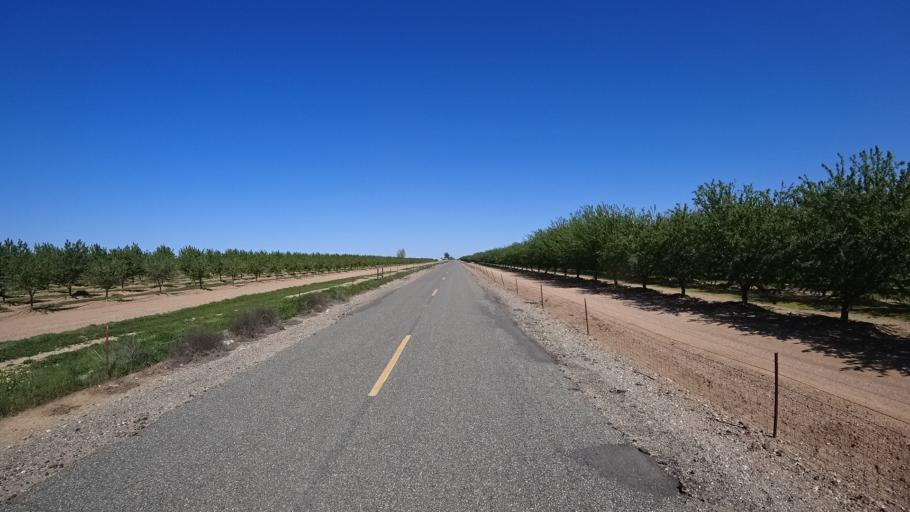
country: US
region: California
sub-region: Glenn County
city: Orland
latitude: 39.6557
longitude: -122.2532
